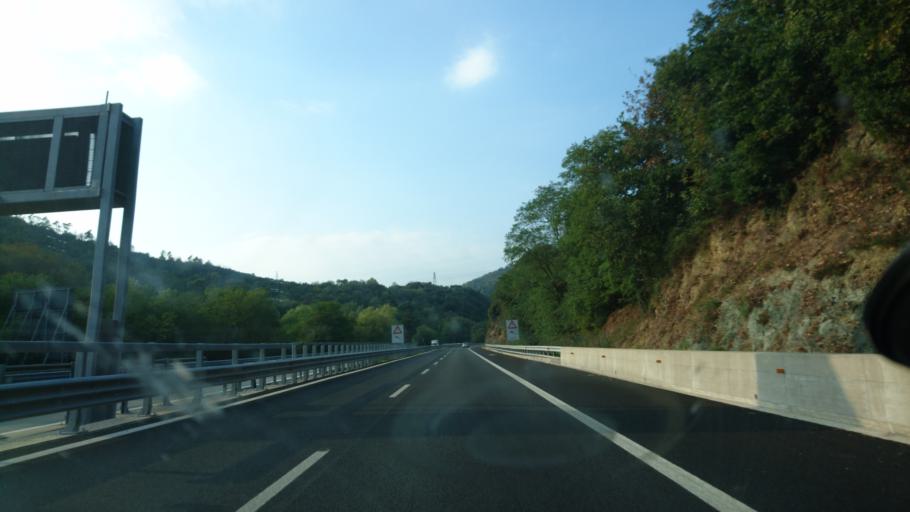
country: IT
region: Liguria
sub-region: Provincia di Savona
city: Valleggia
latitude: 44.2963
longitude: 8.4299
